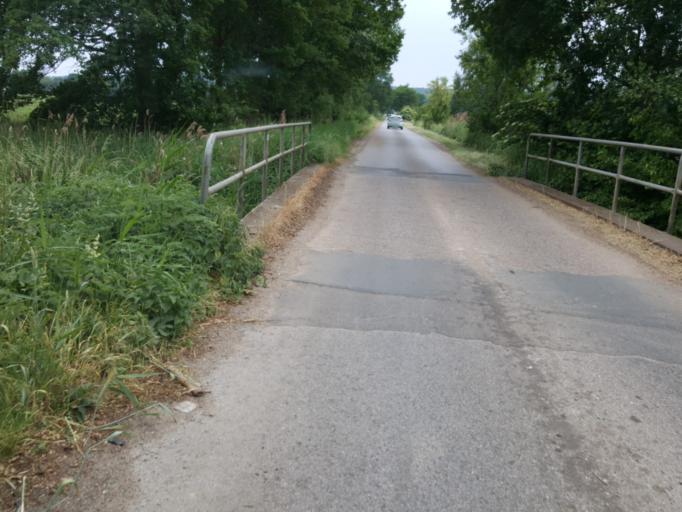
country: DE
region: Lower Saxony
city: Rehburg-Loccum
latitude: 52.4766
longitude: 9.2049
